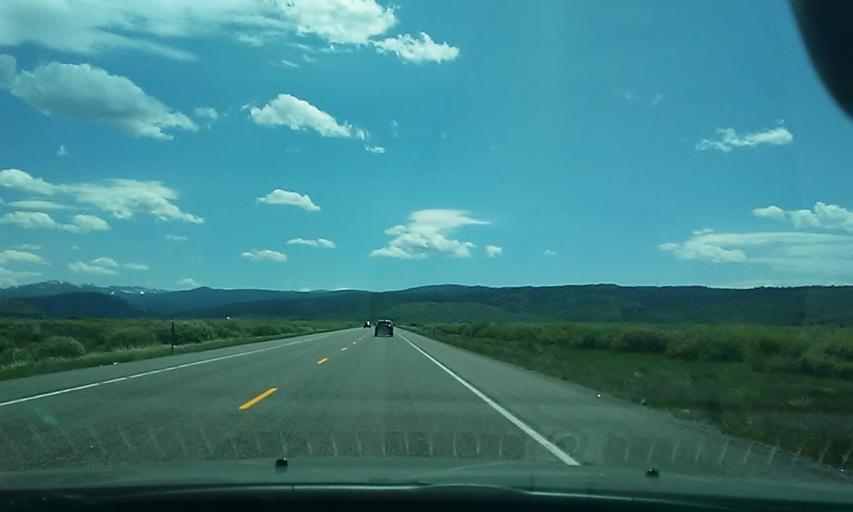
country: US
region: Wyoming
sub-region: Teton County
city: Jackson
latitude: 43.8355
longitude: -110.4314
